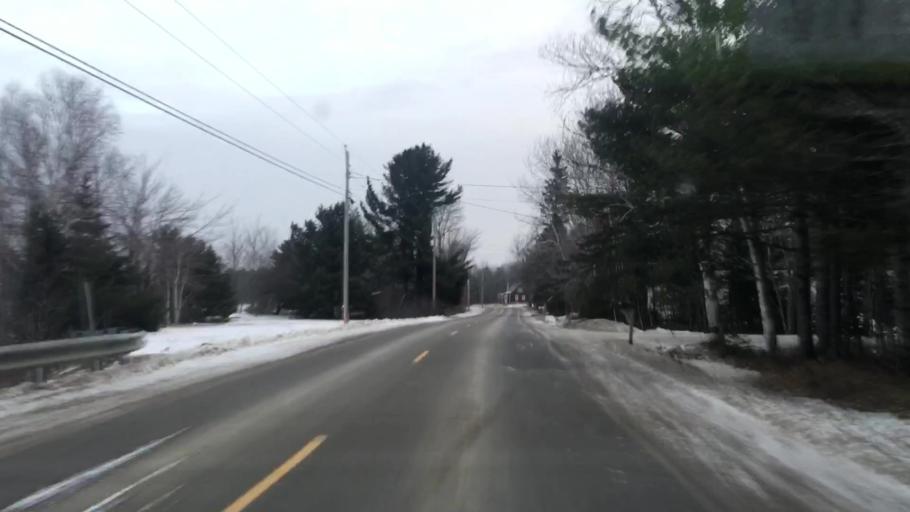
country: US
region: Maine
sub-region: Hancock County
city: Ellsworth
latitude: 44.6107
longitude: -68.3898
